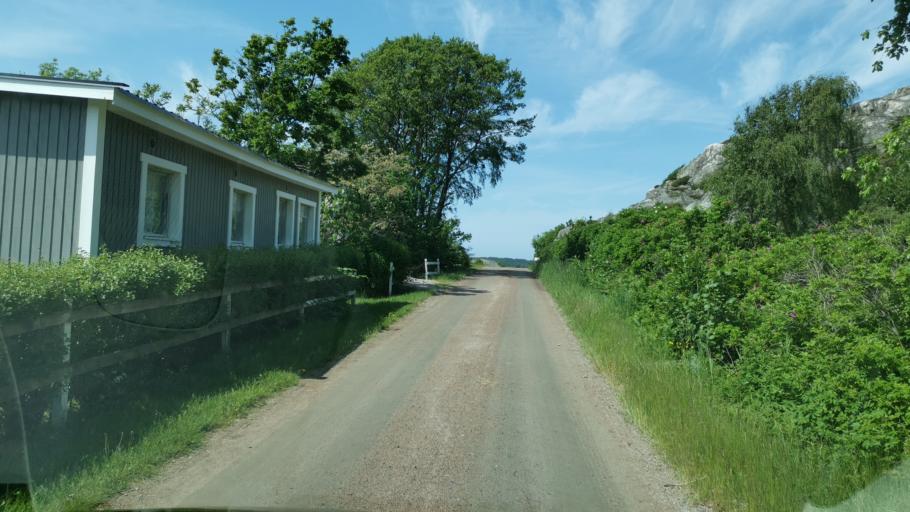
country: SE
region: Vaestra Goetaland
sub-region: Lysekils Kommun
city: Brastad
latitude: 58.2973
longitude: 11.5354
